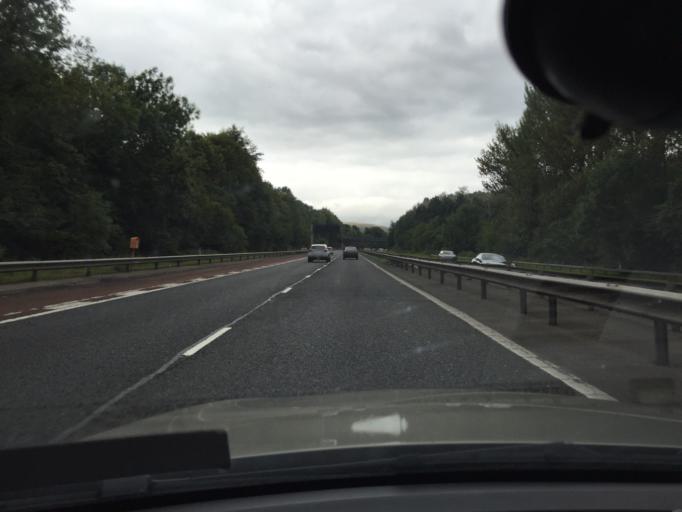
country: GB
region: Northern Ireland
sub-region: Lisburn District
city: Lisburn
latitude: 54.5475
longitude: -5.9952
